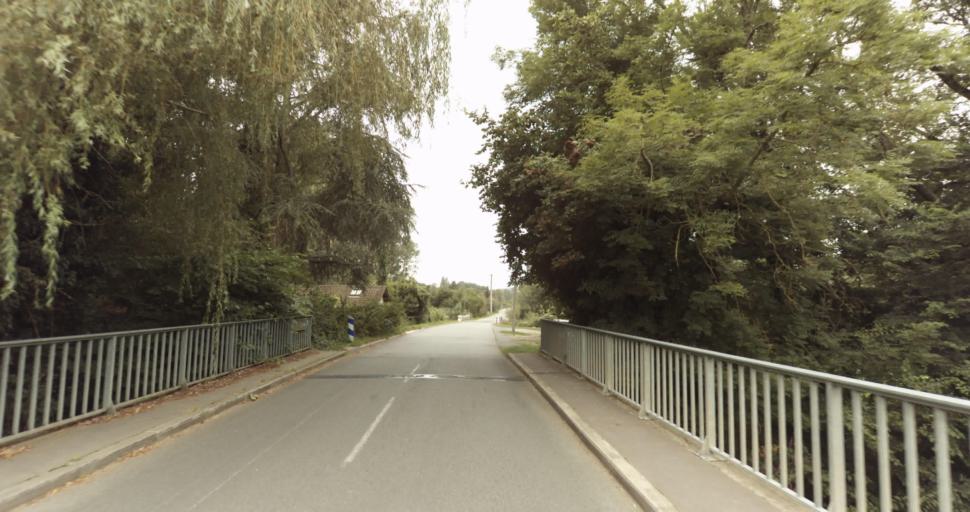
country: FR
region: Haute-Normandie
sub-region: Departement de l'Eure
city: Marcilly-sur-Eure
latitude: 48.8202
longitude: 1.3592
